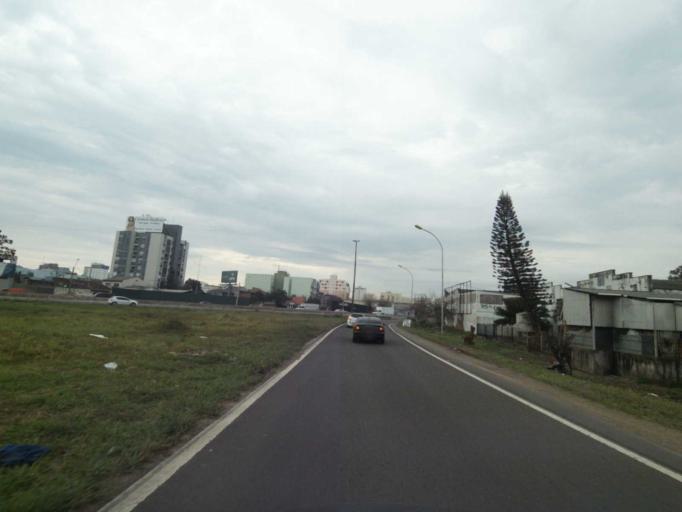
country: BR
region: Rio Grande do Sul
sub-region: Sao Leopoldo
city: Sao Leopoldo
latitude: -29.7620
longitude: -51.1534
